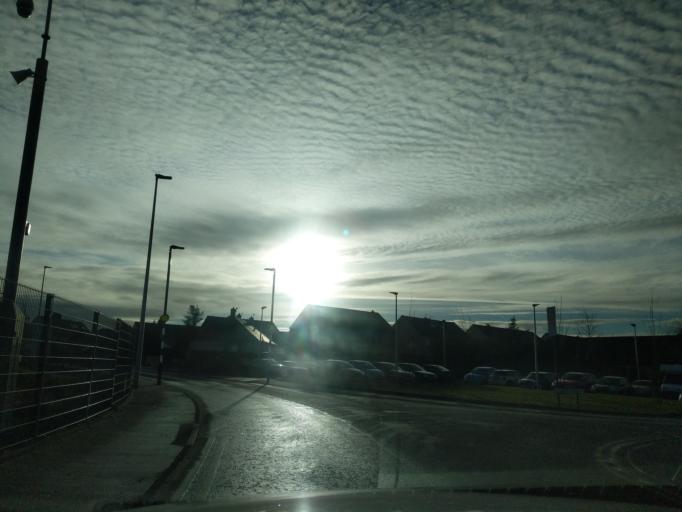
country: GB
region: Scotland
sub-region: Midlothian
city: Loanhead
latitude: 55.8800
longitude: -3.1548
